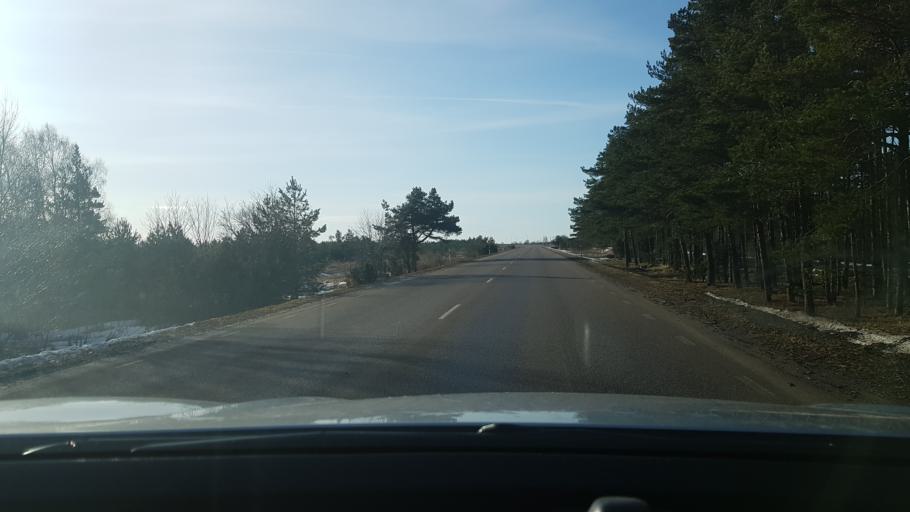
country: EE
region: Saare
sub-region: Kuressaare linn
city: Kuressaare
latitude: 58.2431
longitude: 22.5035
